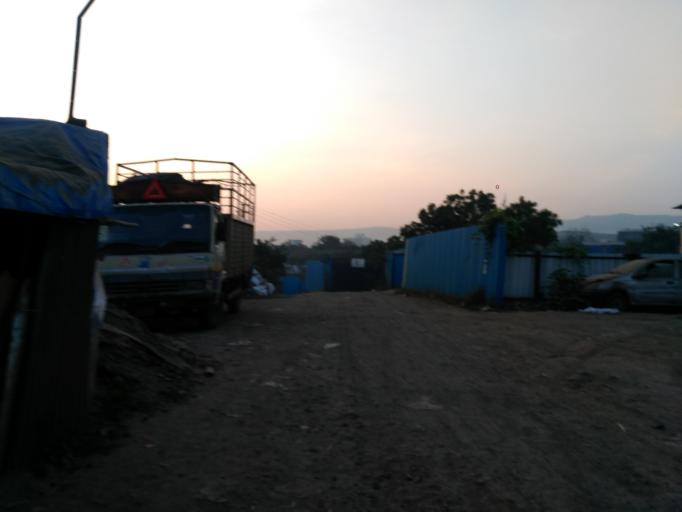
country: IN
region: Maharashtra
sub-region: Pune Division
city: Pune
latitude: 18.4571
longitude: 73.8944
